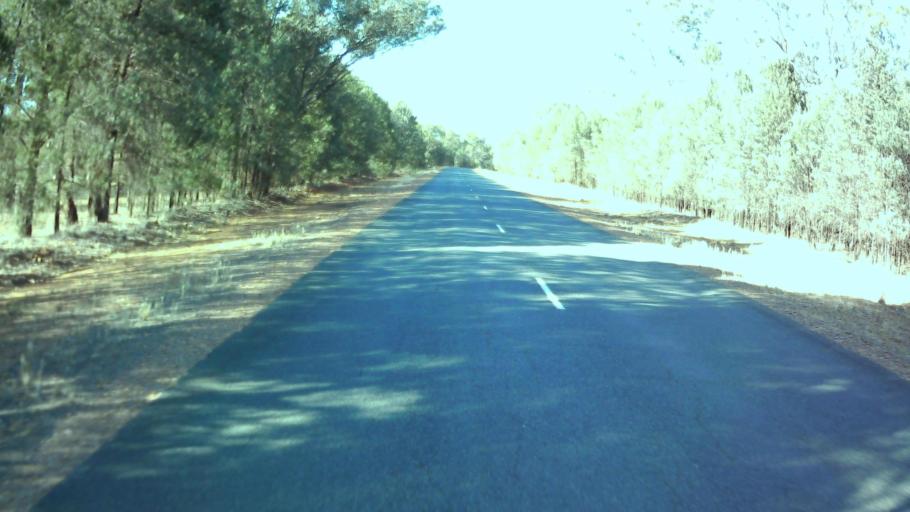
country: AU
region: New South Wales
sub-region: Weddin
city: Grenfell
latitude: -34.0280
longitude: 148.0955
